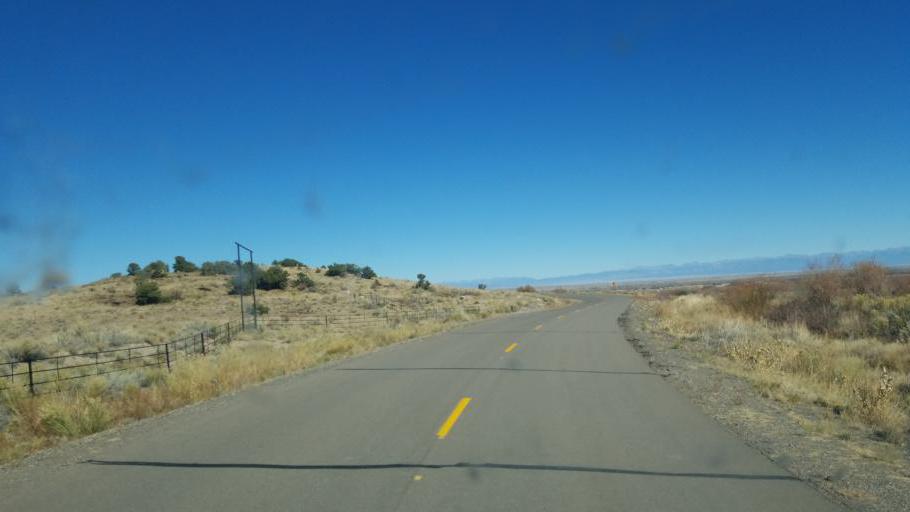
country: US
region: Colorado
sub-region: Rio Grande County
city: Del Norte
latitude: 37.6422
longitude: -106.3646
